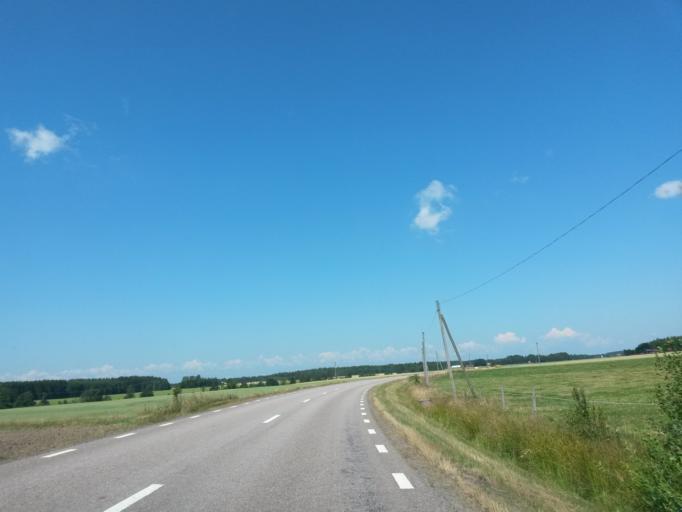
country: SE
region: Vaestra Goetaland
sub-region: Grastorps Kommun
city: Graestorp
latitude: 58.2780
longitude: 12.6762
